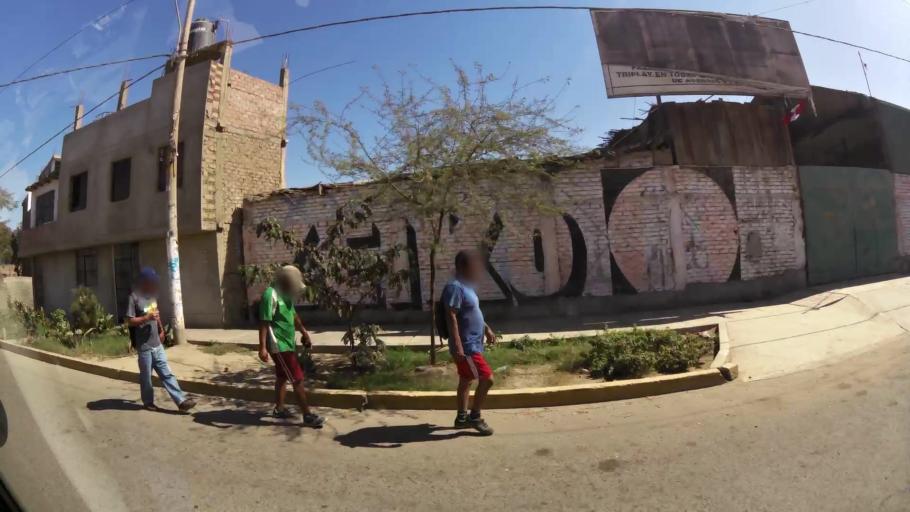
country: PE
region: Ica
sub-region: Provincia de Ica
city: Ica
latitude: -14.0605
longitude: -75.7220
